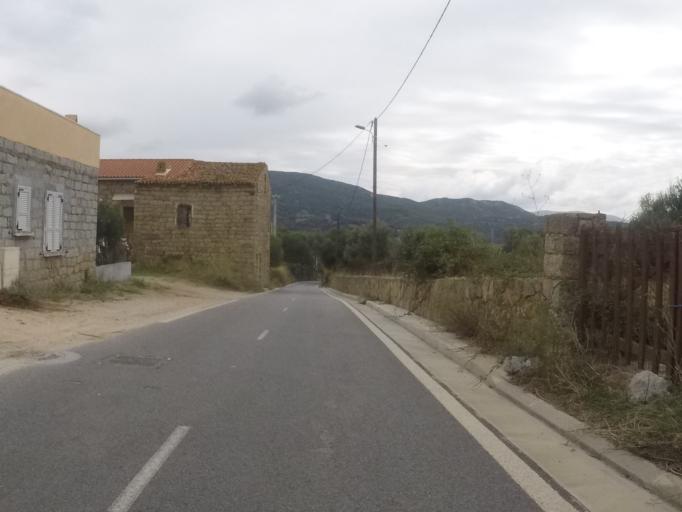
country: FR
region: Corsica
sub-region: Departement de la Corse-du-Sud
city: Olmeto
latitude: 41.7301
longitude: 8.8280
